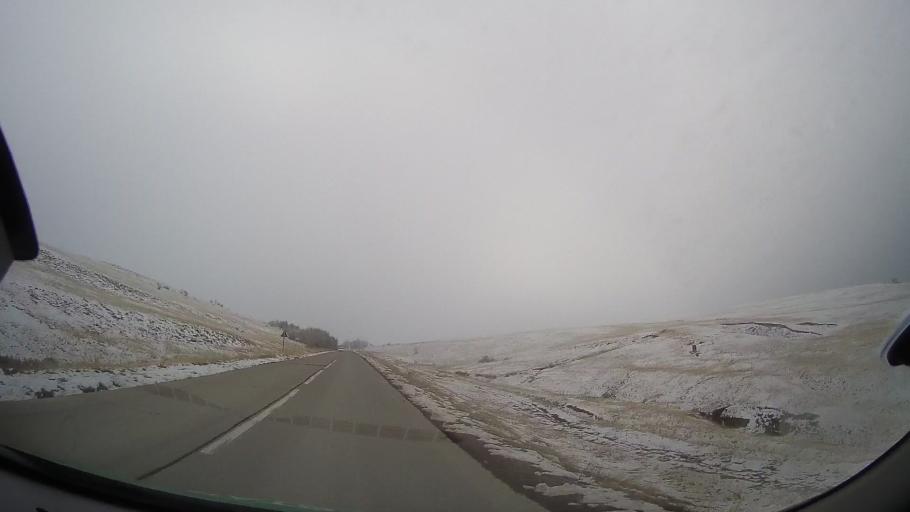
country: RO
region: Vaslui
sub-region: Comuna Ivesti
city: Ivesti
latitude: 46.2093
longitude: 27.5040
